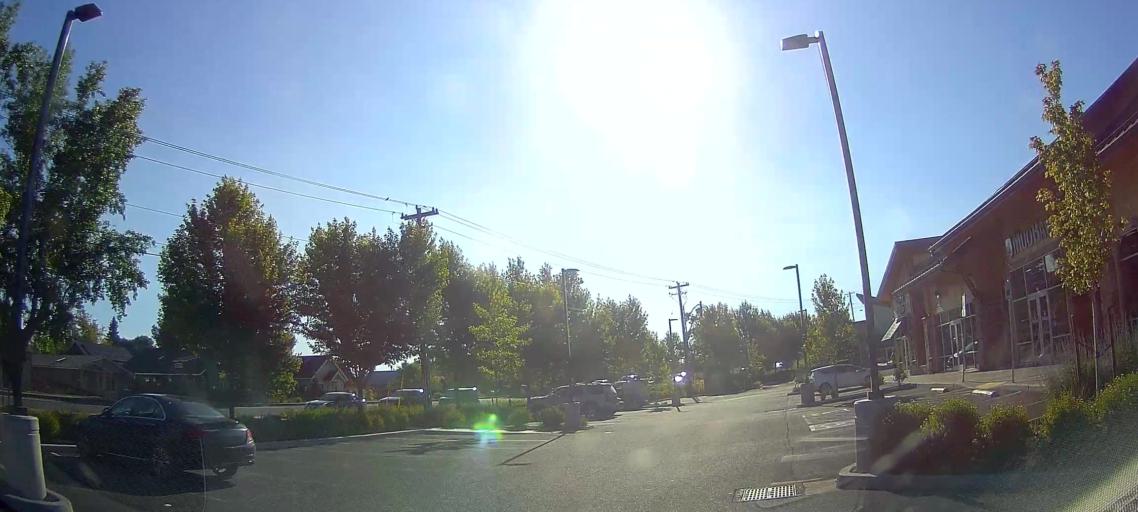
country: US
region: Oregon
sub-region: Deschutes County
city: Bend
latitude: 44.0528
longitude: -121.3107
